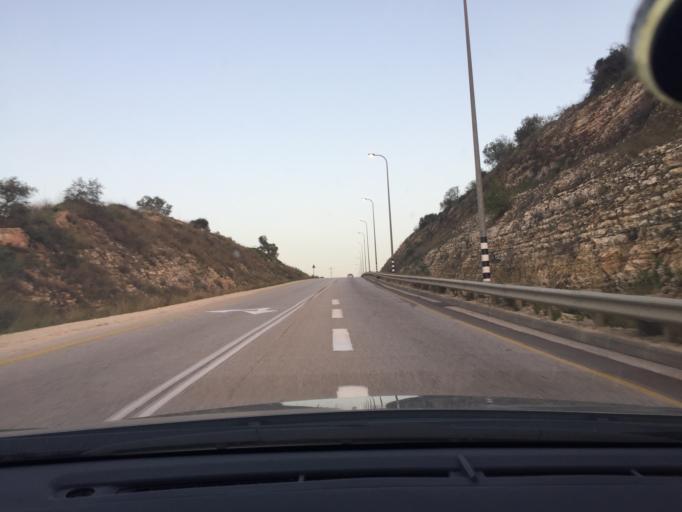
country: PS
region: West Bank
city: Rafat
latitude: 32.0659
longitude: 35.0527
